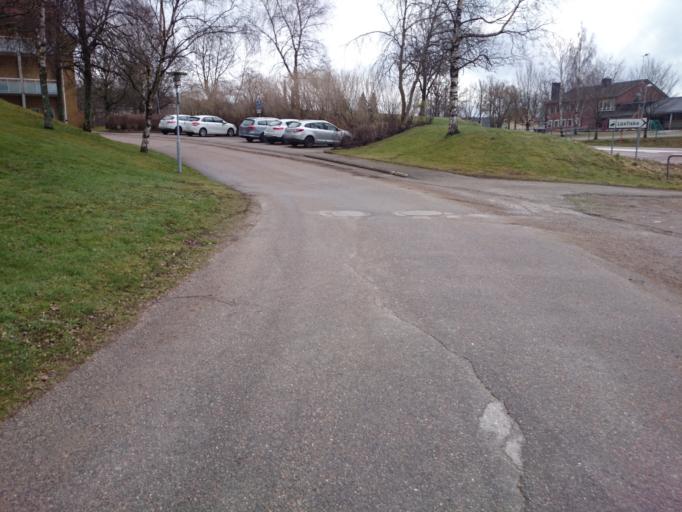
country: SE
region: Vaestra Goetaland
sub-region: Lilla Edets Kommun
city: Lilla Edet
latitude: 58.1337
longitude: 12.1227
